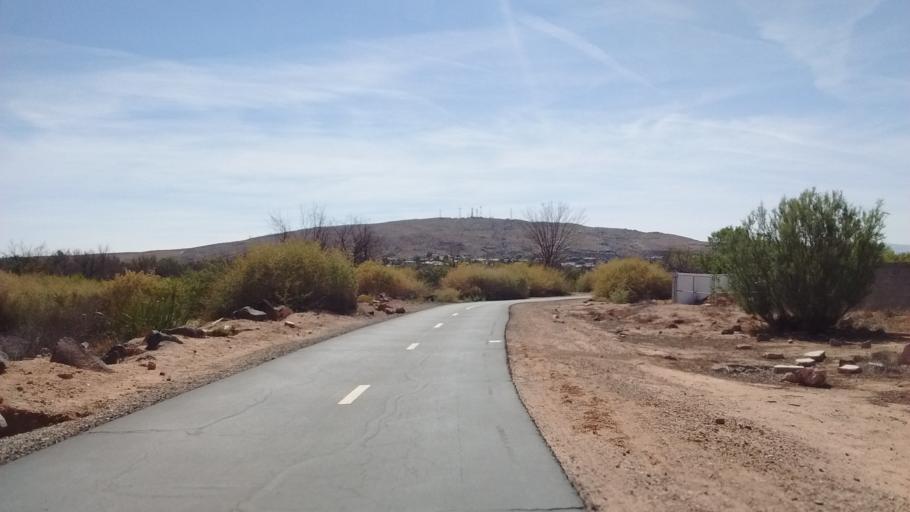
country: US
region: Utah
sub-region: Washington County
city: Saint George
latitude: 37.0844
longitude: -113.5727
